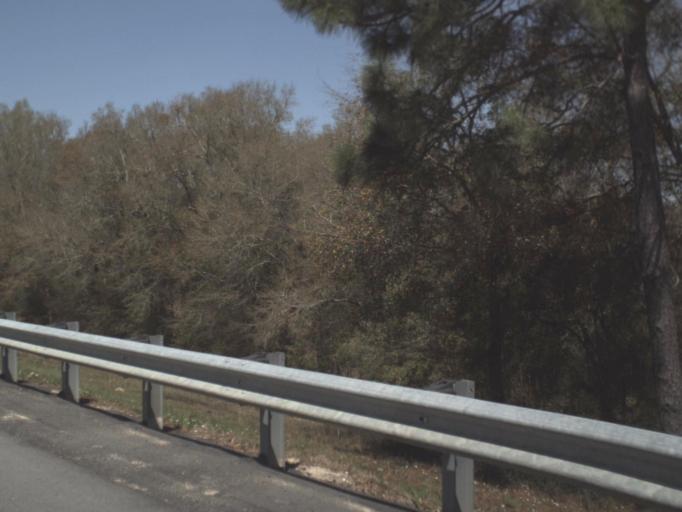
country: US
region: Florida
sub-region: Okaloosa County
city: Crestview
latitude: 30.7376
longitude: -86.3633
